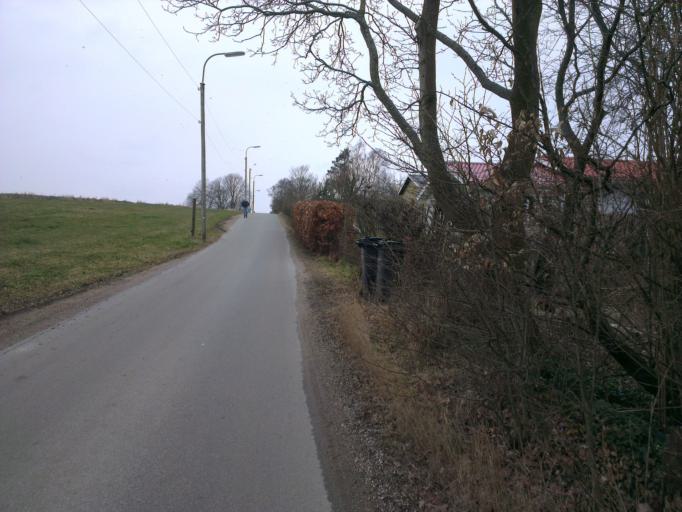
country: DK
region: Capital Region
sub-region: Egedal Kommune
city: Olstykke
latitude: 55.8119
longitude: 12.1131
